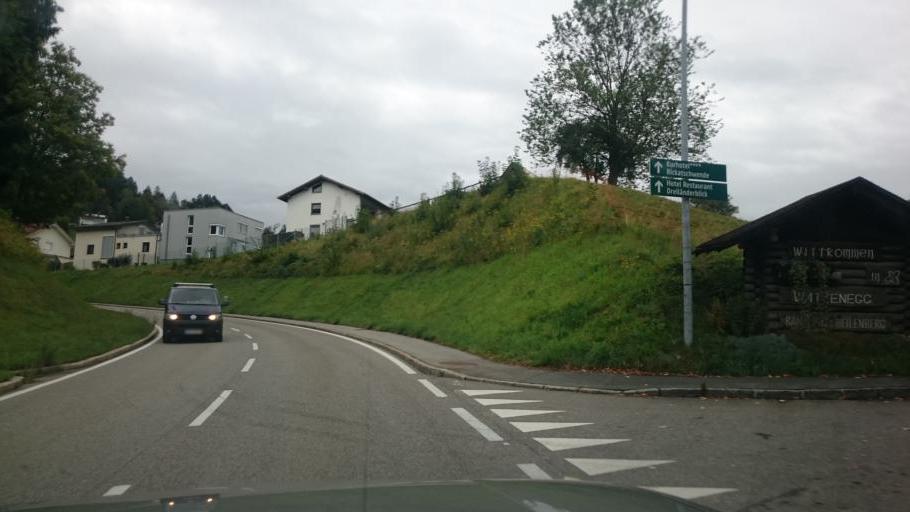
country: AT
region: Vorarlberg
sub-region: Politischer Bezirk Dornbirn
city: Dornbirn
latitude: 47.4123
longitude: 9.7636
